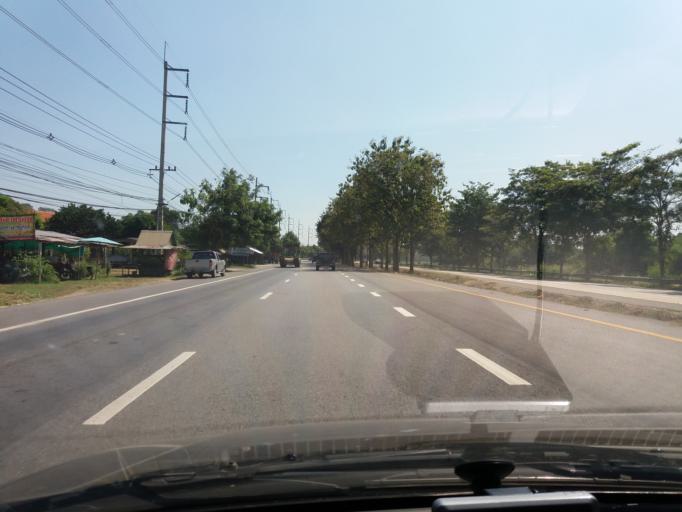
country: TH
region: Chai Nat
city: Chai Nat
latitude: 15.1249
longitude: 100.1484
